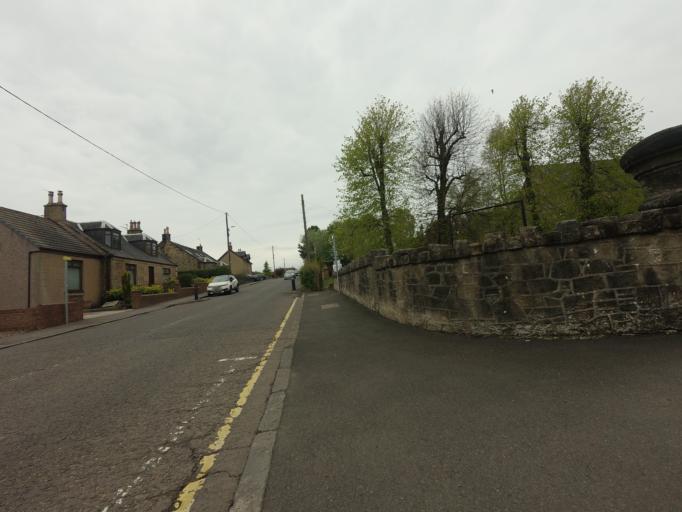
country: GB
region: Scotland
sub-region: Falkirk
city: Polmont
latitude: 55.9806
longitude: -3.7408
